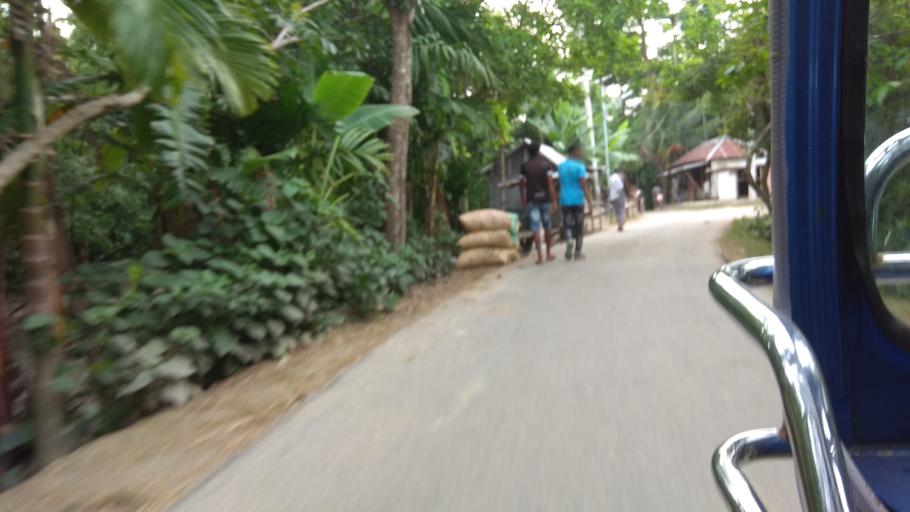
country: BD
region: Khulna
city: Kalia
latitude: 23.0383
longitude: 89.6622
